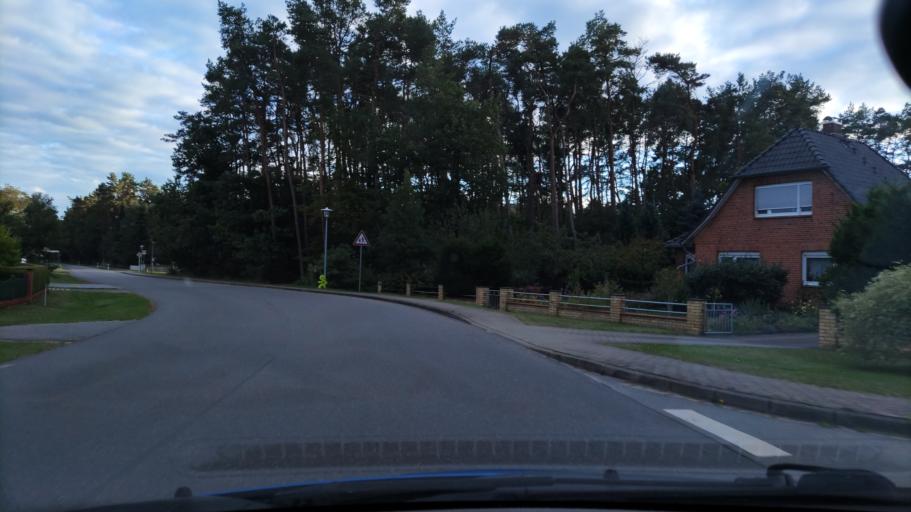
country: DE
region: Mecklenburg-Vorpommern
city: Boizenburg
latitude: 53.3746
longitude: 10.8563
